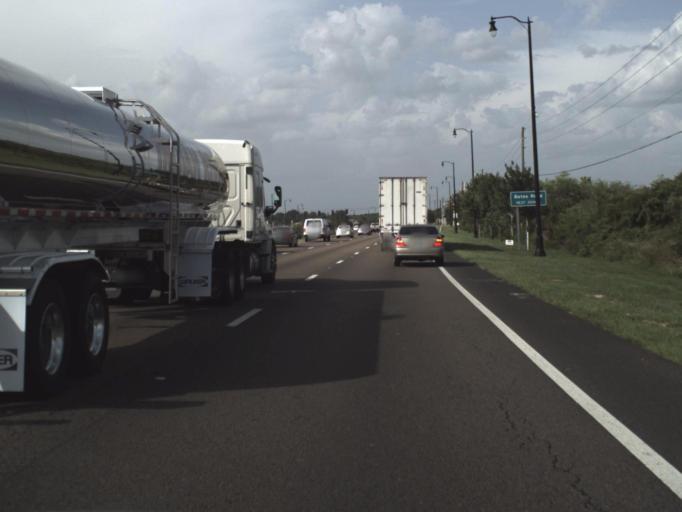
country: US
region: Florida
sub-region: Polk County
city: Haines City
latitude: 28.1353
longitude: -81.6388
